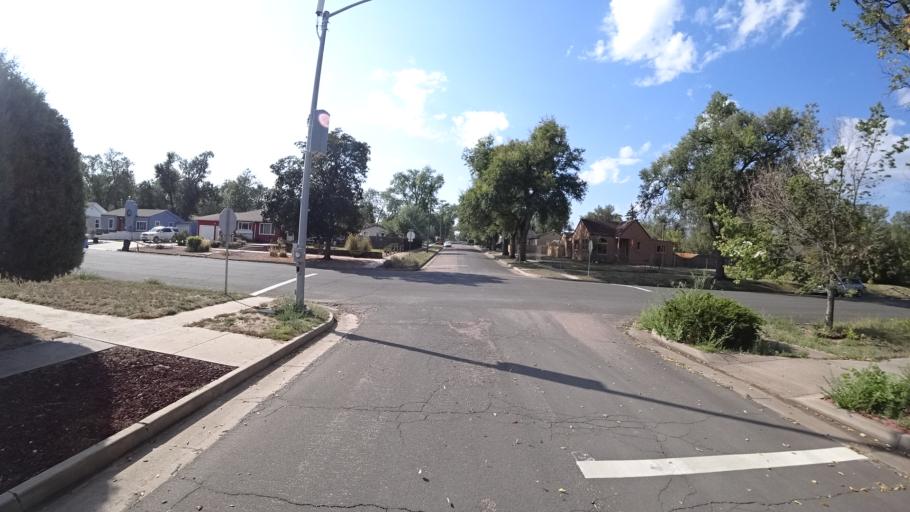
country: US
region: Colorado
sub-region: El Paso County
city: Colorado Springs
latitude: 38.8292
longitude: -104.8058
